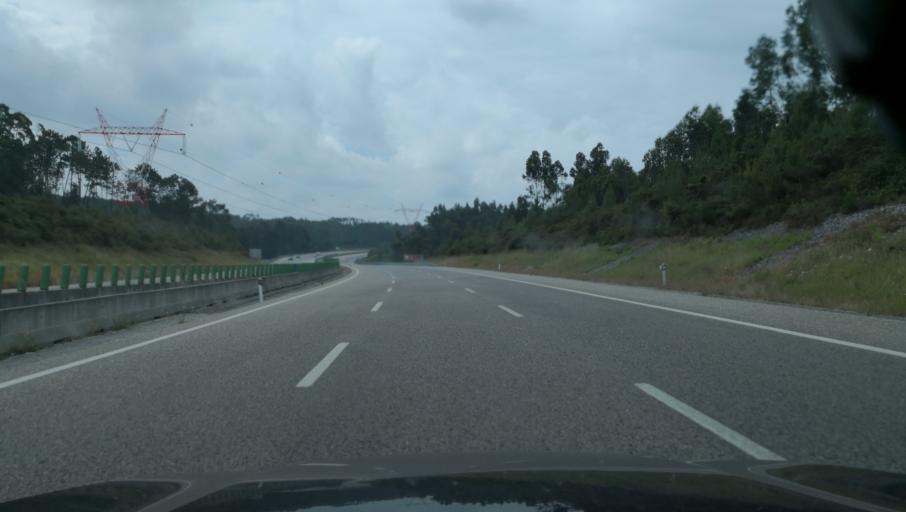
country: PT
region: Leiria
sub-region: Pombal
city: Lourical
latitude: 39.9560
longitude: -8.7742
